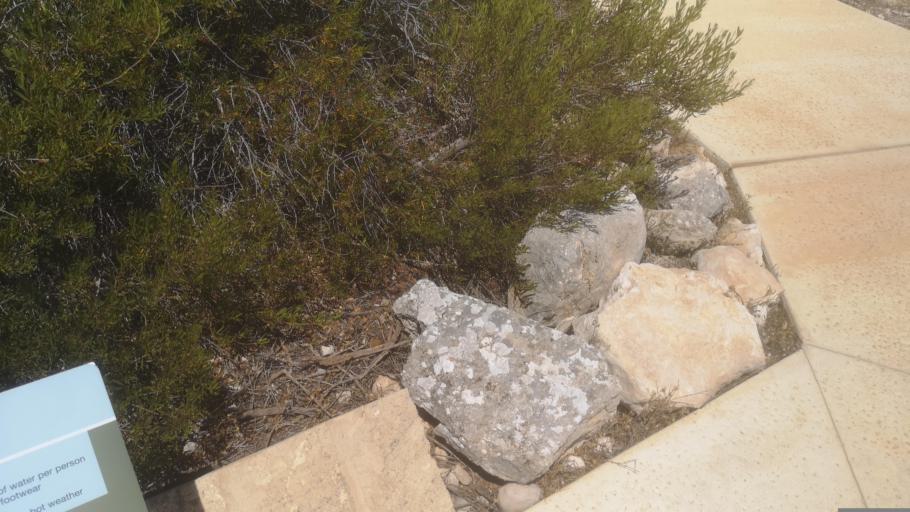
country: AU
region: Western Australia
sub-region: Northampton Shire
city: Kalbarri
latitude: -27.6980
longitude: 114.2165
